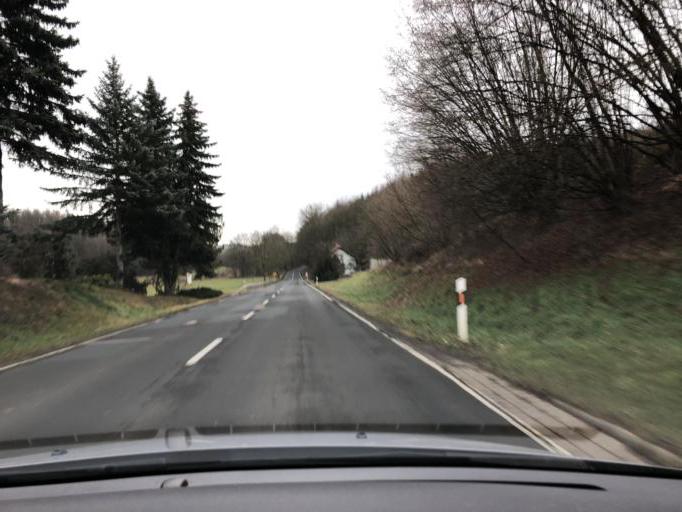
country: DE
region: Saxony
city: Ebersbach
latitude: 51.0984
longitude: 13.1328
